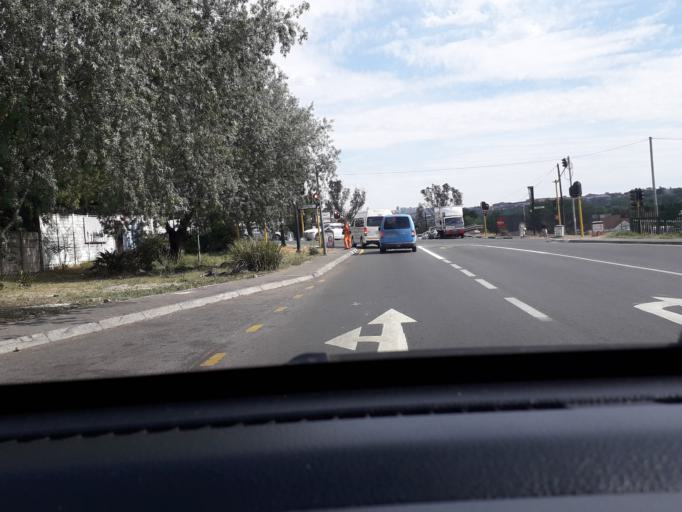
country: ZA
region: Gauteng
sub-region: City of Johannesburg Metropolitan Municipality
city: Midrand
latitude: -26.0388
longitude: 28.0701
